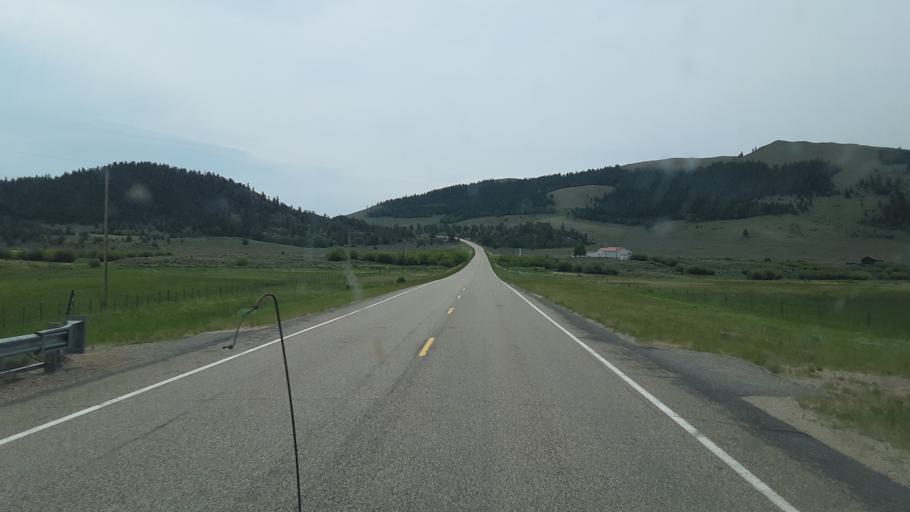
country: US
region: Colorado
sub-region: Jackson County
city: Walden
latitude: 40.9352
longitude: -106.3406
